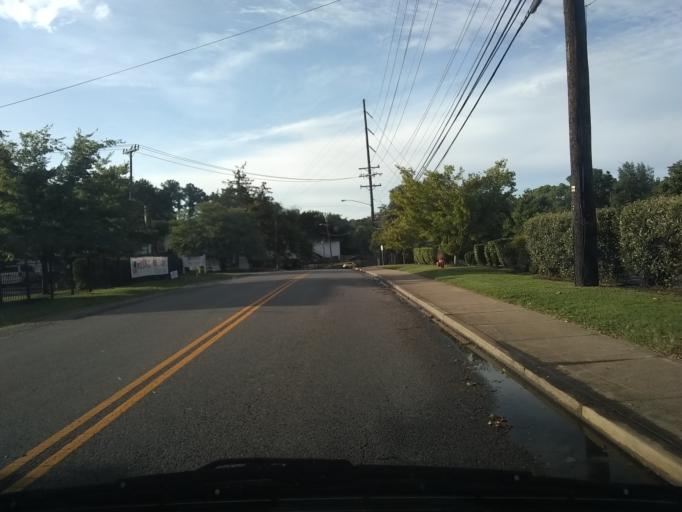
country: US
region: Tennessee
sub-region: Davidson County
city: Nashville
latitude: 36.1283
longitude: -86.7072
